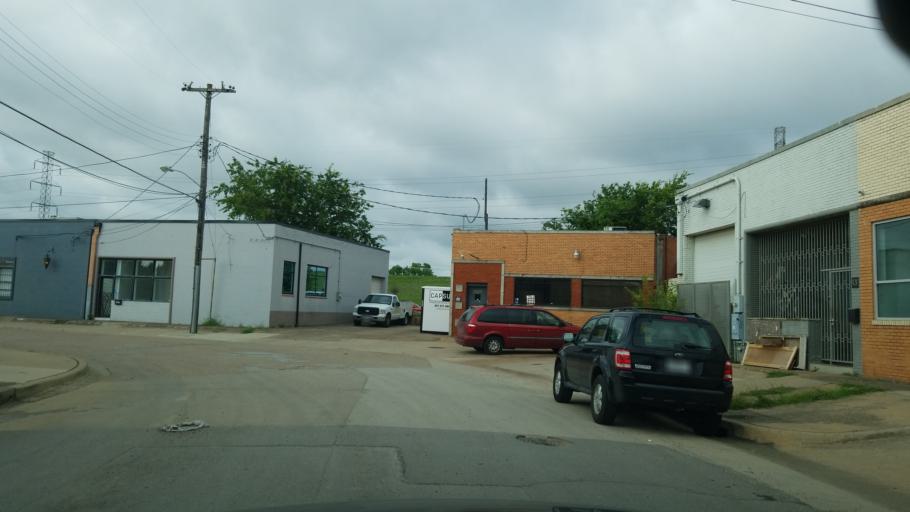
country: US
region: Texas
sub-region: Dallas County
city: Dallas
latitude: 32.7931
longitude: -96.8308
